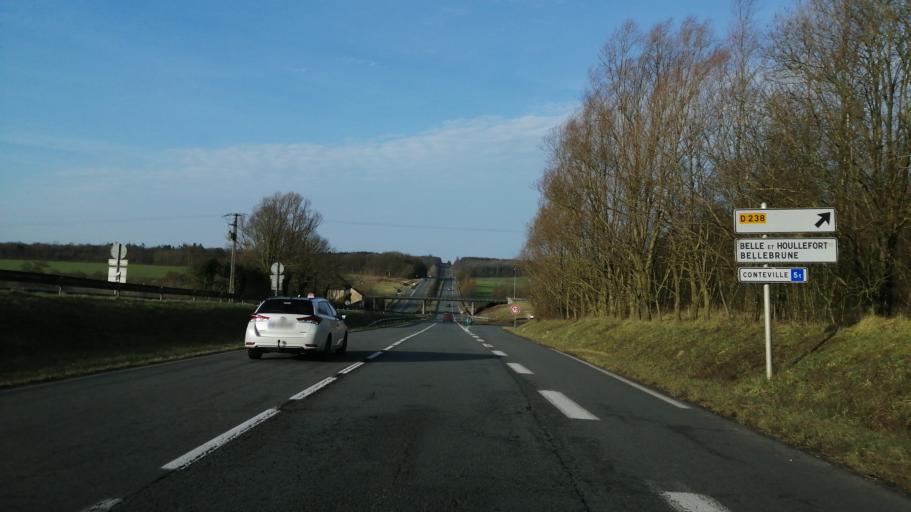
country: FR
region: Nord-Pas-de-Calais
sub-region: Departement du Pas-de-Calais
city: Rety
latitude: 50.7372
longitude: 1.7704
